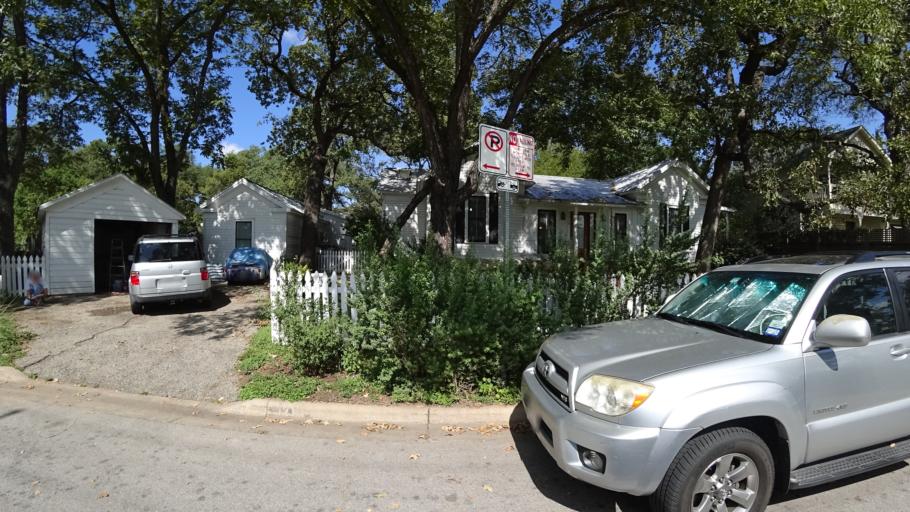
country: US
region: Texas
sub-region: Travis County
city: Austin
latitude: 30.3073
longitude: -97.7446
